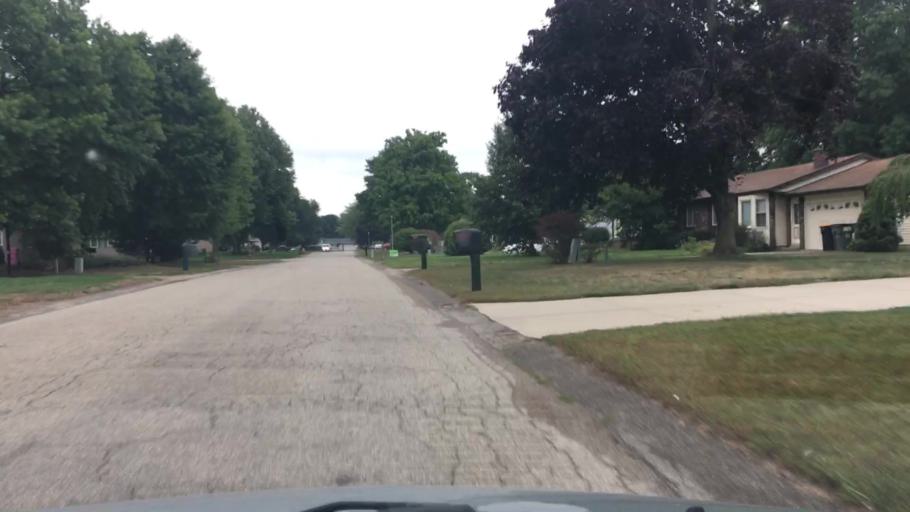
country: US
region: Michigan
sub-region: Ottawa County
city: Hudsonville
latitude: 42.9004
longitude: -85.8491
